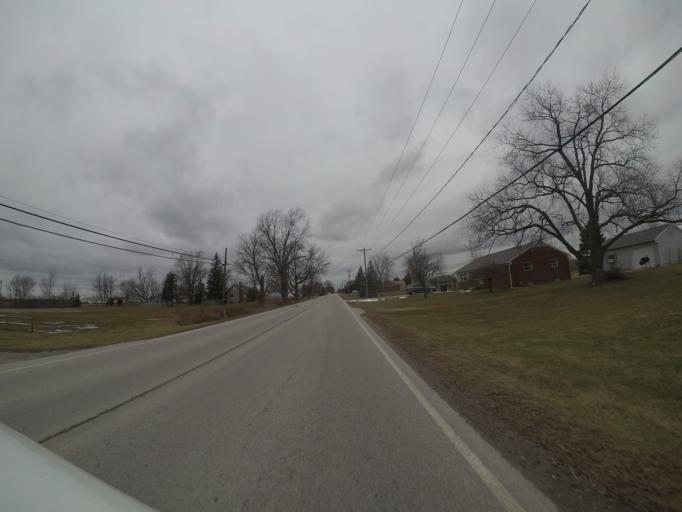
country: US
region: Ohio
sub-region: Wood County
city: Walbridge
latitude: 41.5704
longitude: -83.5123
